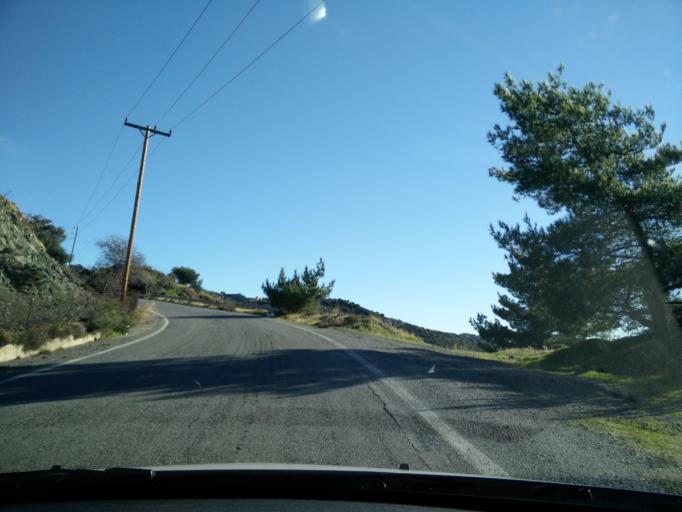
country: GR
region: Crete
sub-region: Nomos Lasithiou
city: Gra Liyia
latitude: 35.0308
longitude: 25.5020
